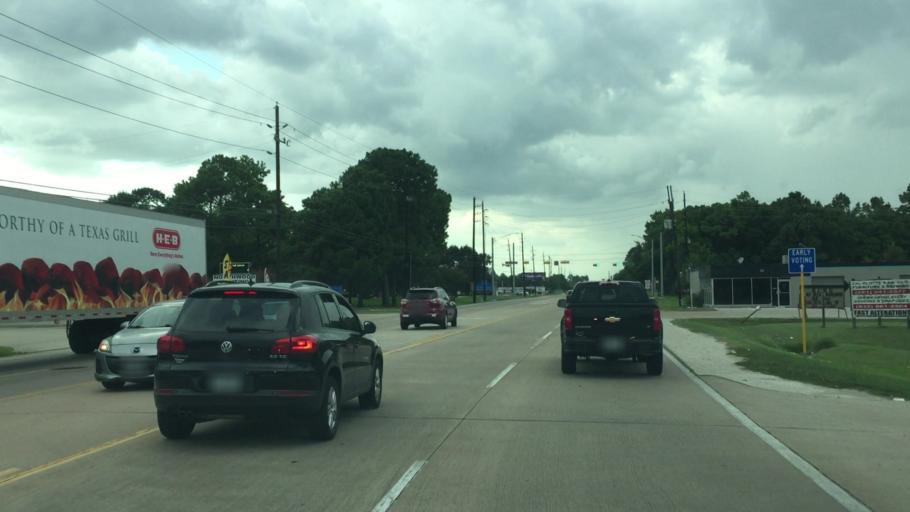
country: US
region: Texas
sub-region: Harris County
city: Hudson
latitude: 29.9908
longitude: -95.5005
